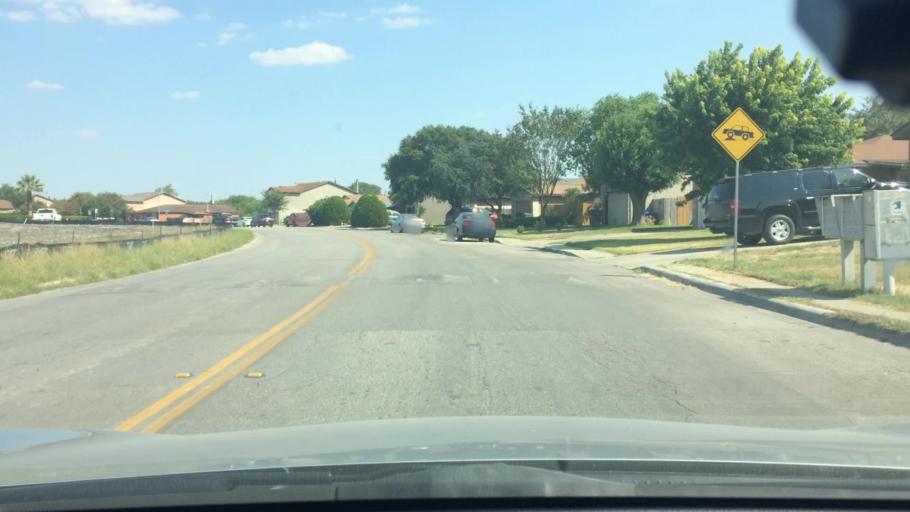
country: US
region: Texas
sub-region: Bexar County
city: Kirby
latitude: 29.4693
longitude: -98.3737
